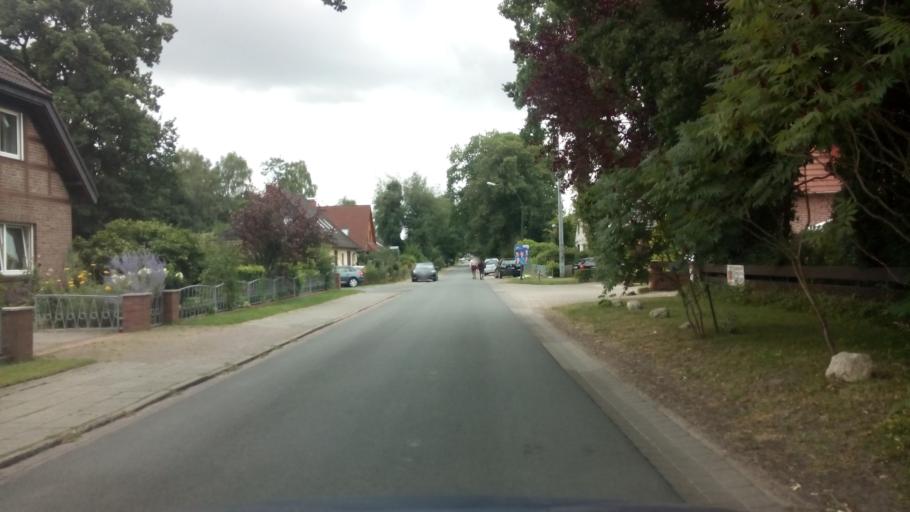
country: DE
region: Lower Saxony
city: Ritterhude
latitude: 53.2081
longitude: 8.7512
